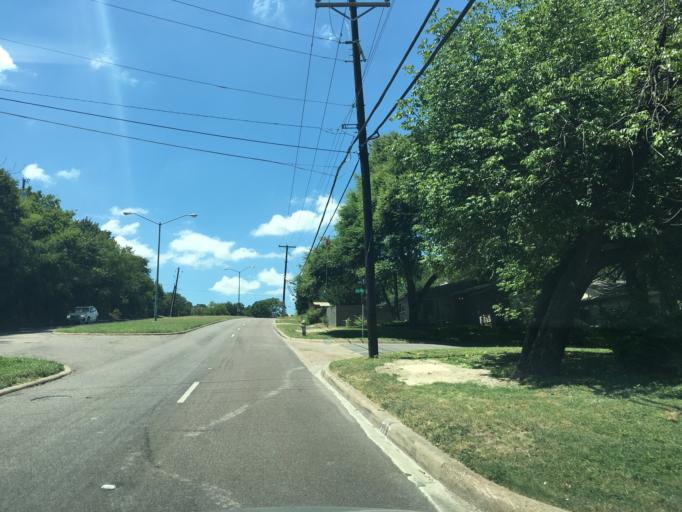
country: US
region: Texas
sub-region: Dallas County
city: Garland
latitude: 32.8469
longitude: -96.6954
